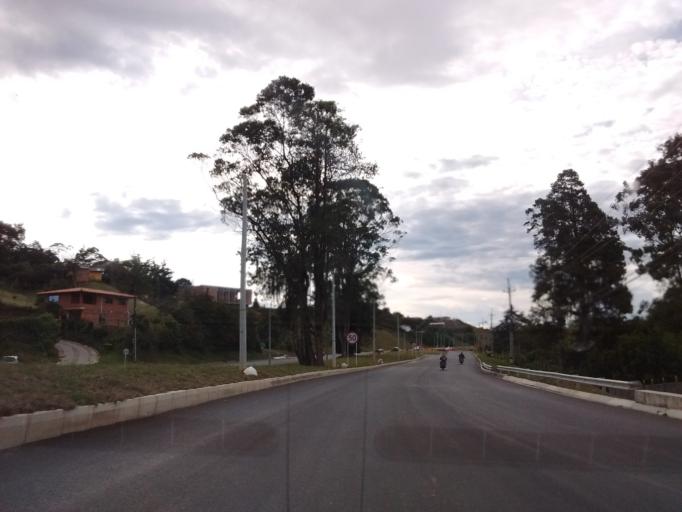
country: CO
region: Antioquia
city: Santuario
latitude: 6.1350
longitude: -75.2940
